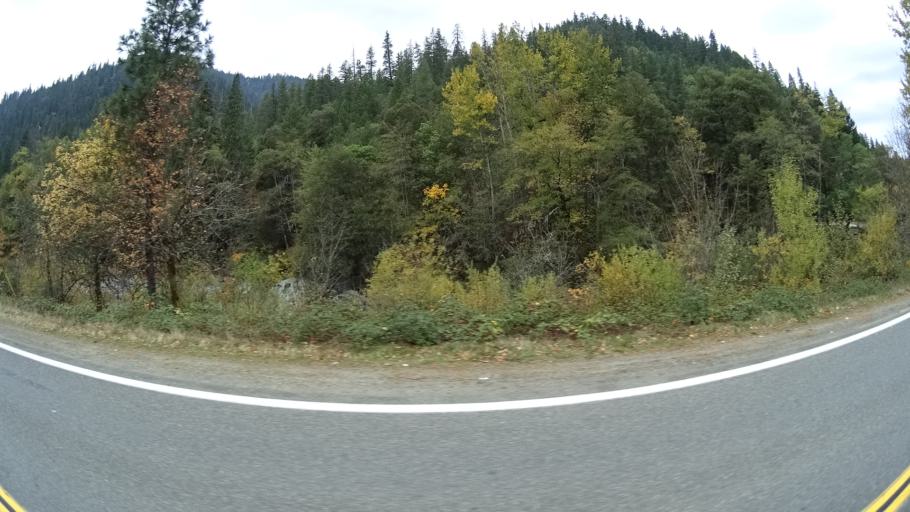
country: US
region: California
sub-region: Siskiyou County
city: Happy Camp
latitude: 41.8494
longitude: -123.3886
